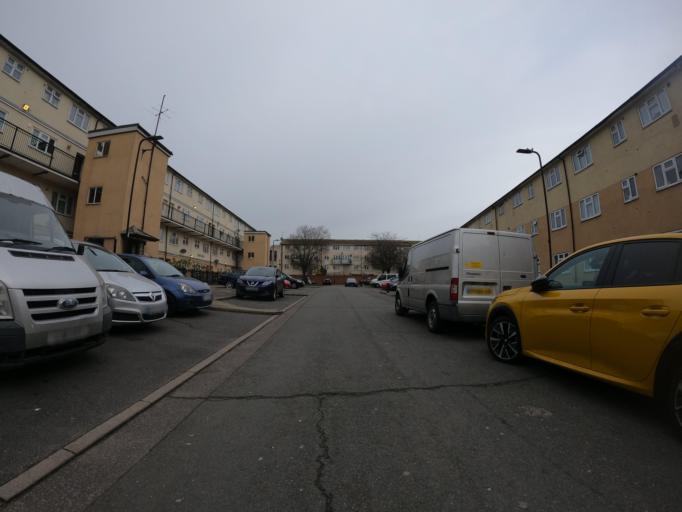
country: GB
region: England
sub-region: Greater London
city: Greenford
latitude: 51.5168
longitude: -0.3570
